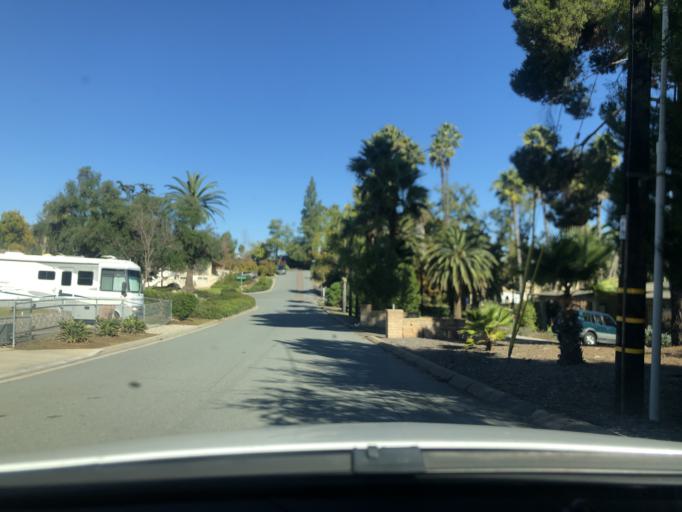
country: US
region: California
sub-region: San Diego County
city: Casa de Oro-Mount Helix
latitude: 32.7718
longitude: -116.9451
